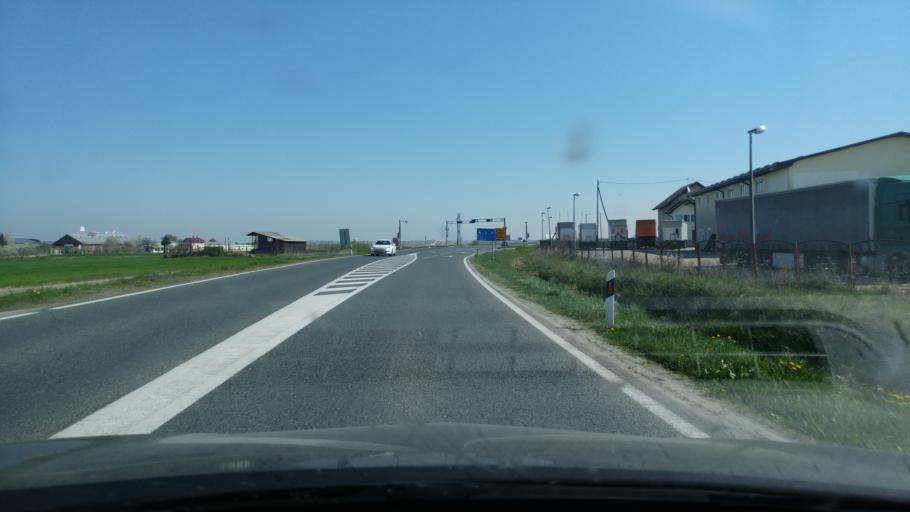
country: HR
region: Osjecko-Baranjska
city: Viskovci
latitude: 45.3302
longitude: 18.3939
